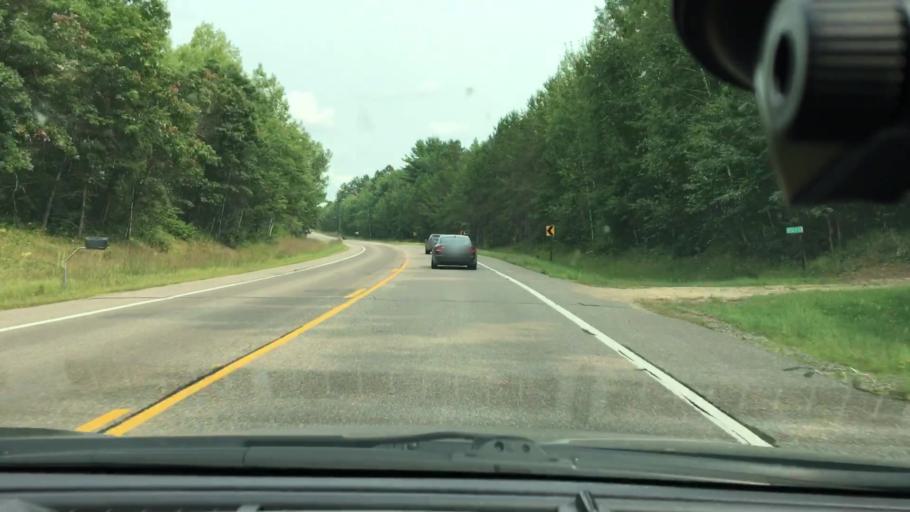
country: US
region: Minnesota
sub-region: Crow Wing County
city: Cross Lake
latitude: 46.7309
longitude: -93.9981
